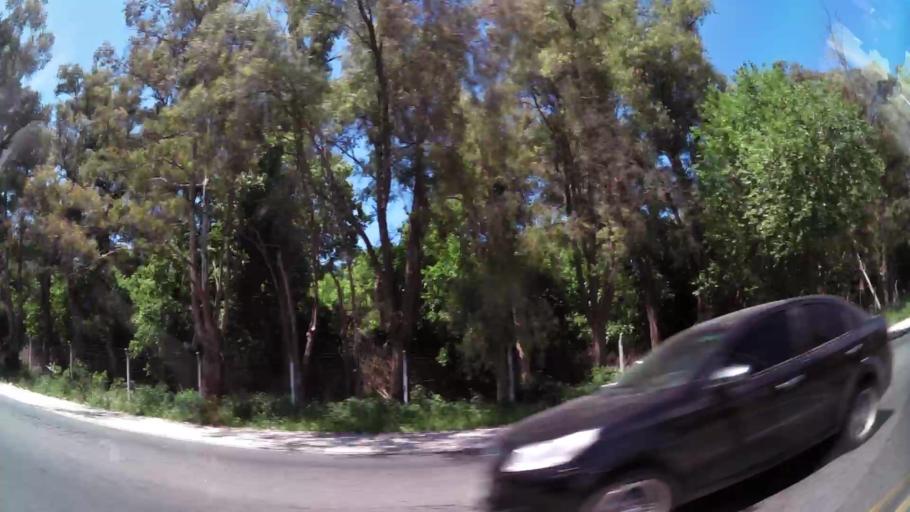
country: AR
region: Buenos Aires
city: Hurlingham
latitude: -34.5225
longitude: -58.6778
